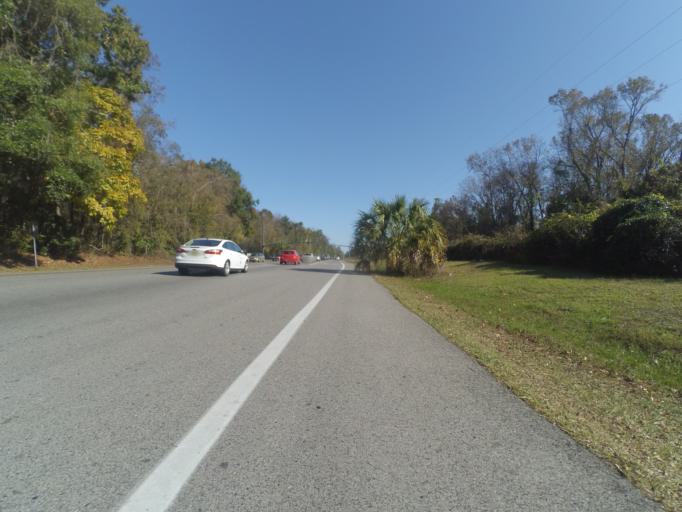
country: US
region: Florida
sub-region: Alachua County
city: Gainesville
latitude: 29.6398
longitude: -82.3995
